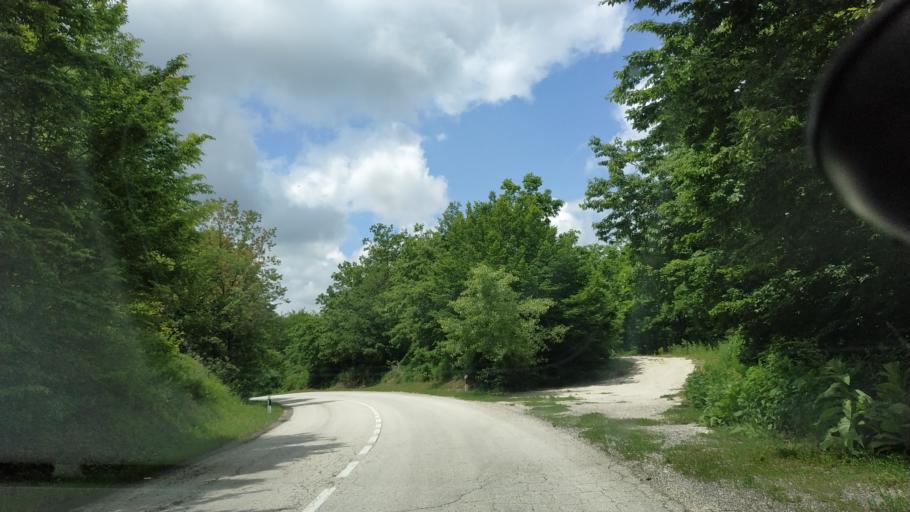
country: RS
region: Central Serbia
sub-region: Borski Okrug
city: Bor
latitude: 44.0869
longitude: 22.0005
